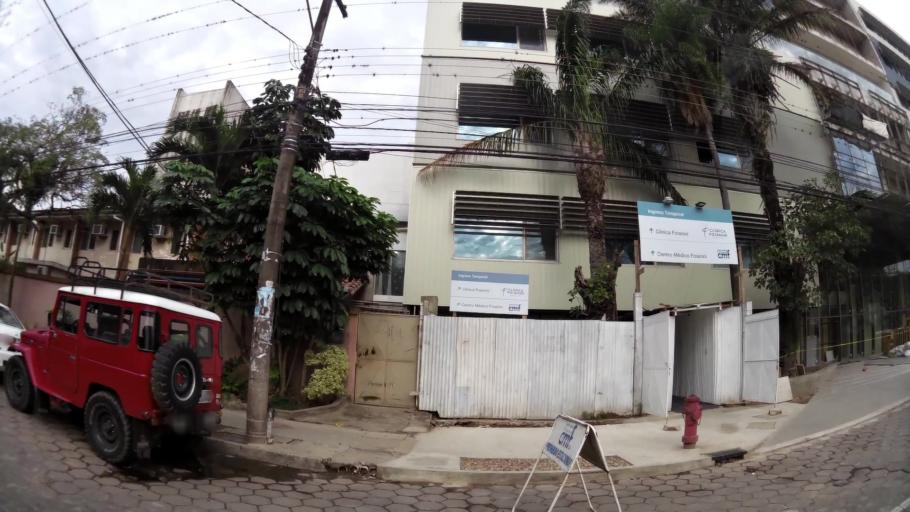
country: BO
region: Santa Cruz
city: Santa Cruz de la Sierra
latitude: -17.7916
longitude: -63.1797
